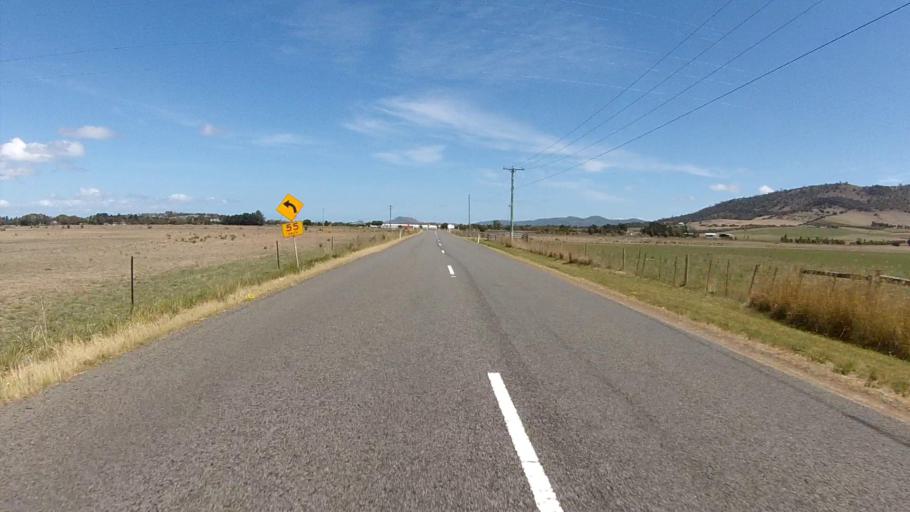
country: AU
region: Tasmania
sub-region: Sorell
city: Sorell
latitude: -42.7659
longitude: 147.5162
